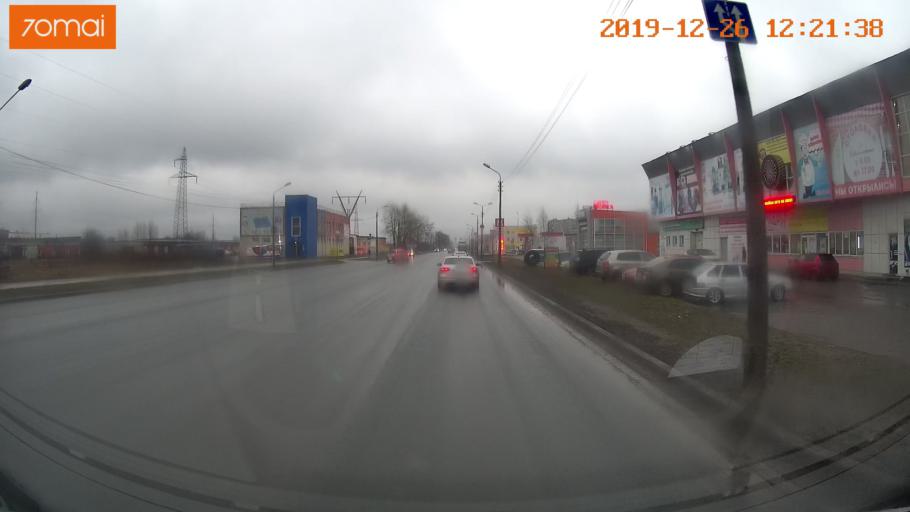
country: RU
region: Vologda
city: Cherepovets
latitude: 59.1516
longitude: 37.9332
